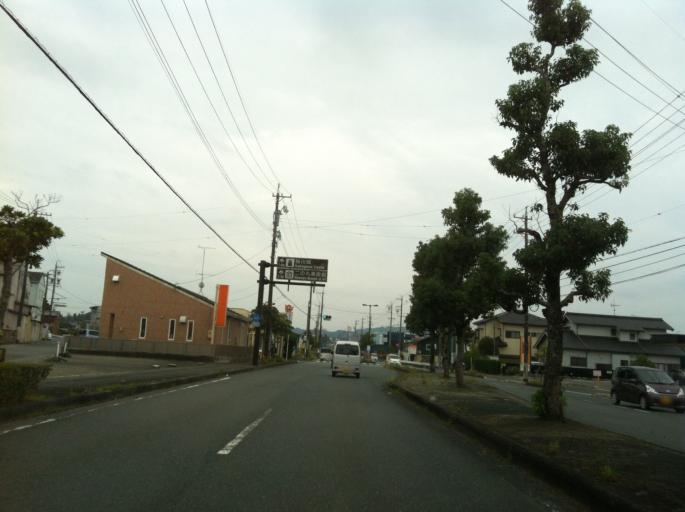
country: JP
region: Shizuoka
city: Kakegawa
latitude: 34.7868
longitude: 138.0130
